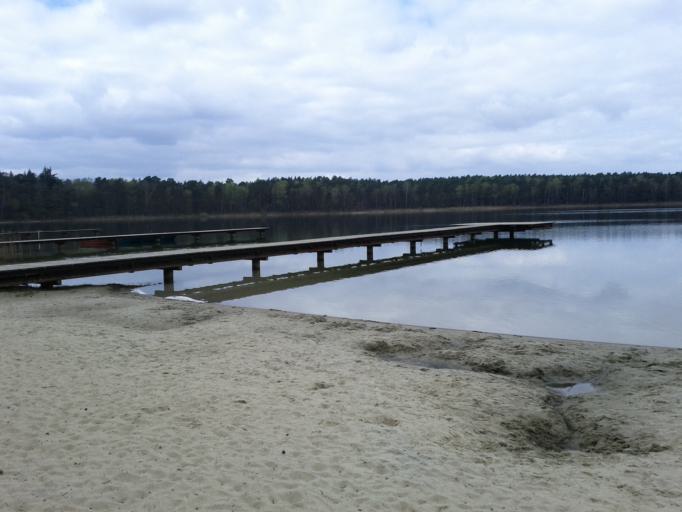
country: DE
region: Brandenburg
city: Spreenhagen
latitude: 52.3815
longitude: 13.8499
